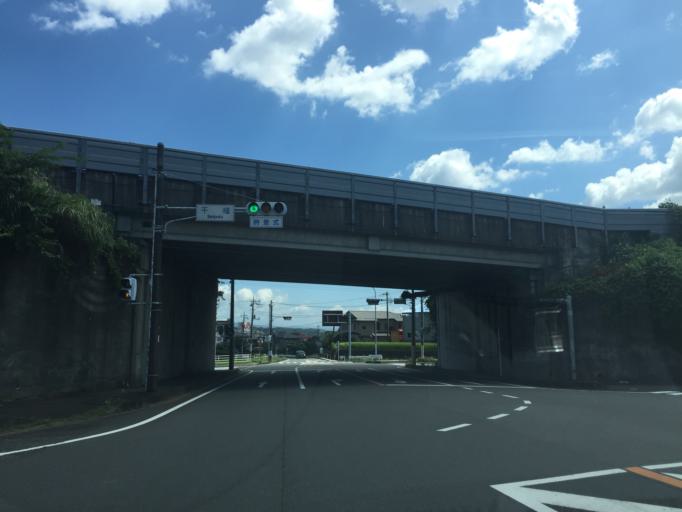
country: JP
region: Shizuoka
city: Mishima
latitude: 35.1906
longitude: 138.9068
